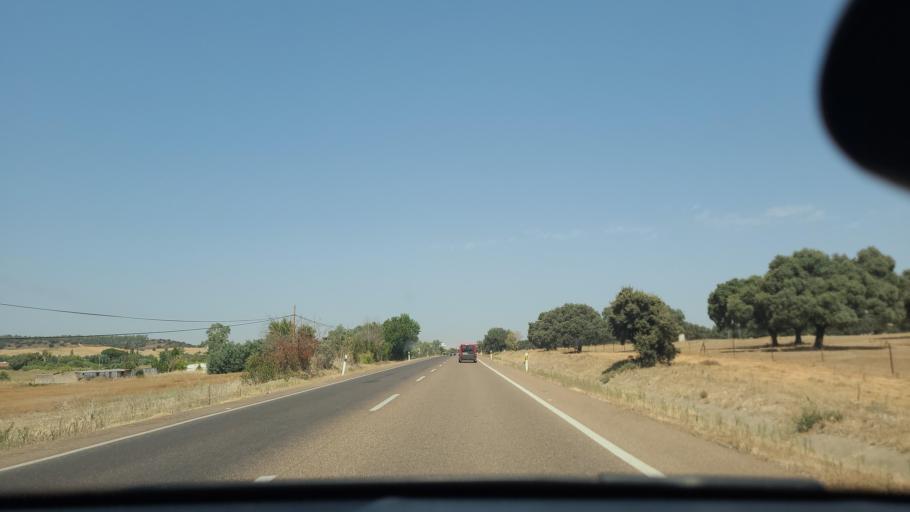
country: ES
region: Extremadura
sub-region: Provincia de Badajoz
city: Badajoz
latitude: 38.8387
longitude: -6.9269
